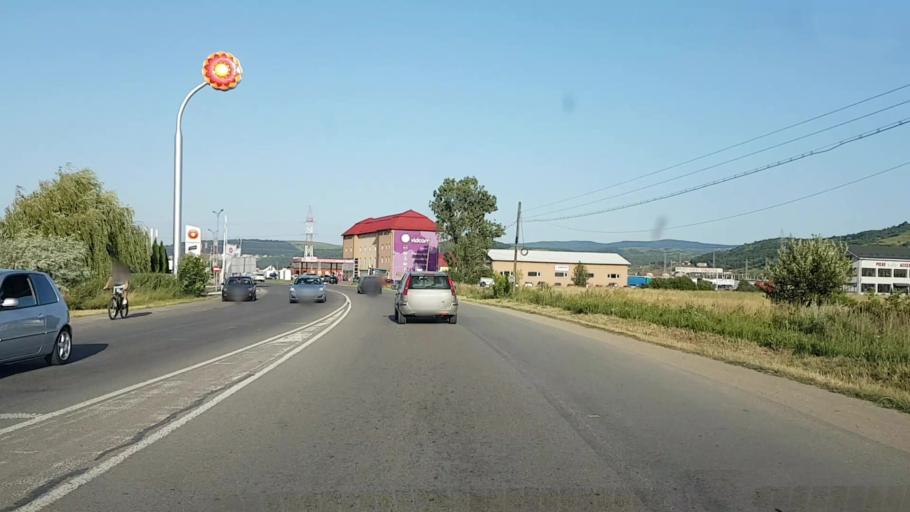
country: RO
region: Cluj
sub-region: Comuna Floresti
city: Luna de Sus
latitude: 46.7447
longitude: 23.4534
